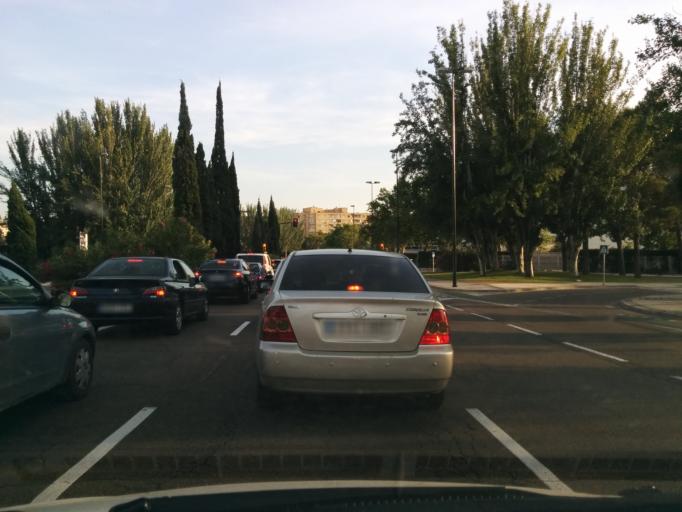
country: ES
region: Aragon
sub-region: Provincia de Zaragoza
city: Zaragoza
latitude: 41.6510
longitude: -0.8637
